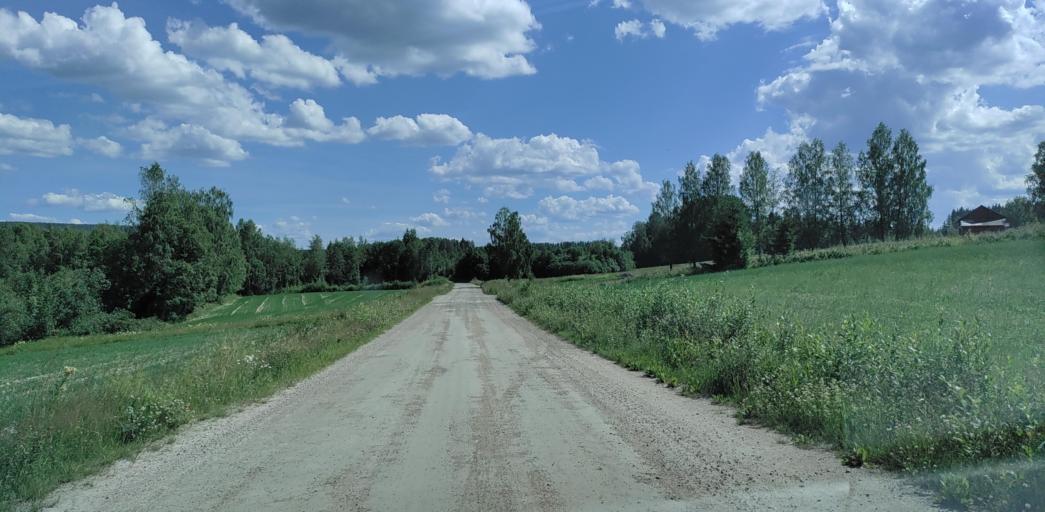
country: SE
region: Vaermland
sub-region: Hagfors Kommun
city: Ekshaerad
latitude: 60.1266
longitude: 13.4765
